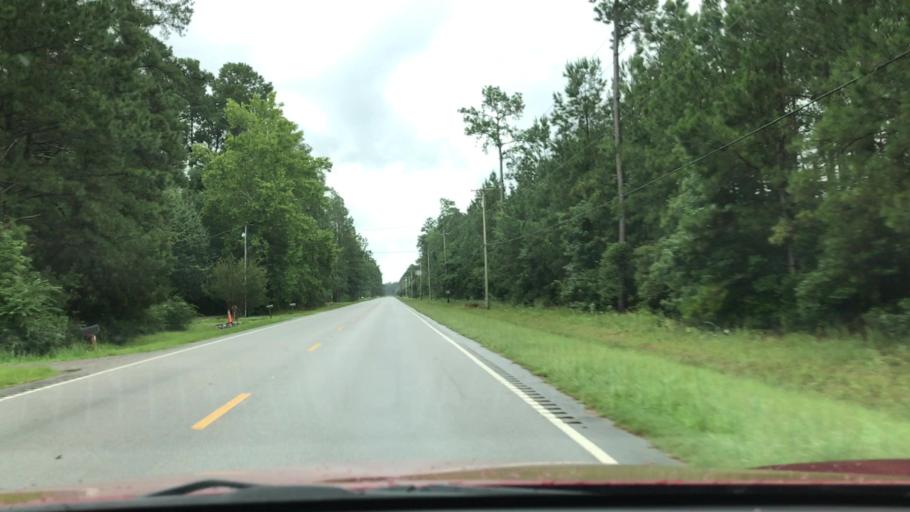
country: US
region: South Carolina
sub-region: Horry County
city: Conway
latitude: 33.7850
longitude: -79.0751
